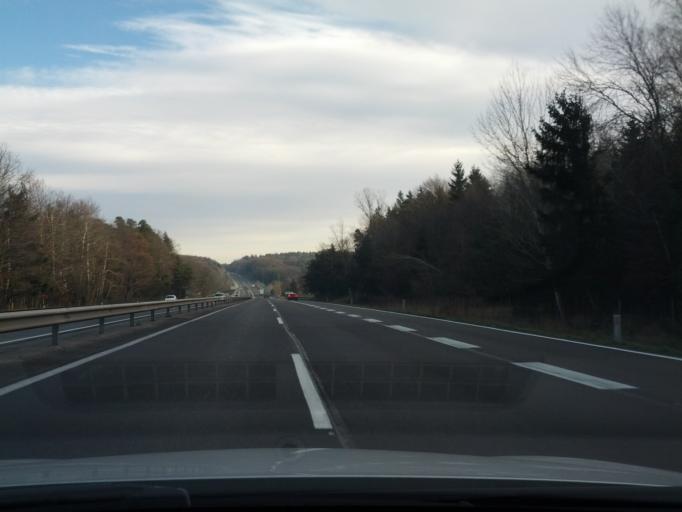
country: SI
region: Slovenska Bistrica
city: Slovenska Bistrica
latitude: 46.3944
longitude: 15.5966
